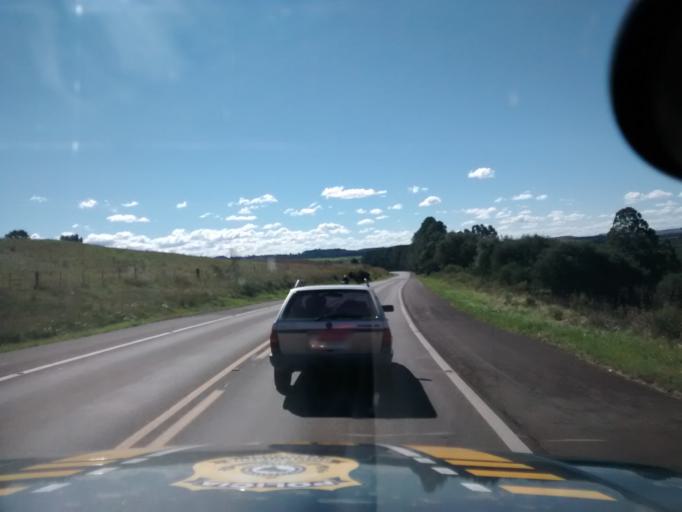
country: BR
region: Rio Grande do Sul
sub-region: Vacaria
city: Vacaria
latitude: -28.3517
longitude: -51.1429
